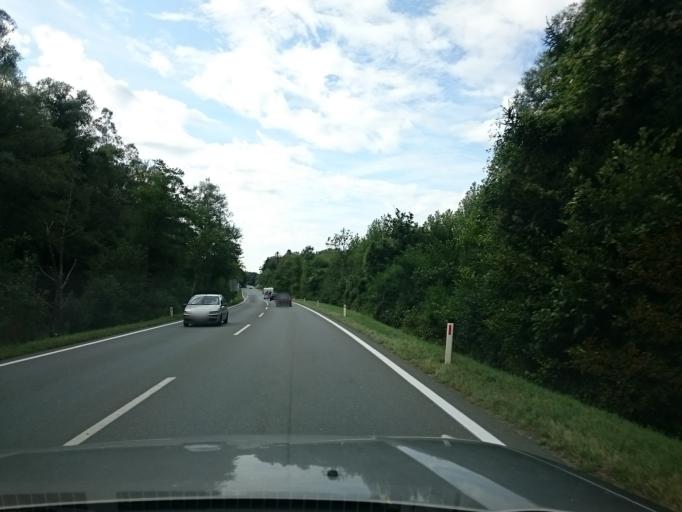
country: DE
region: Bavaria
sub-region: Upper Bavaria
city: Laufen
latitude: 47.9303
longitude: 12.9672
